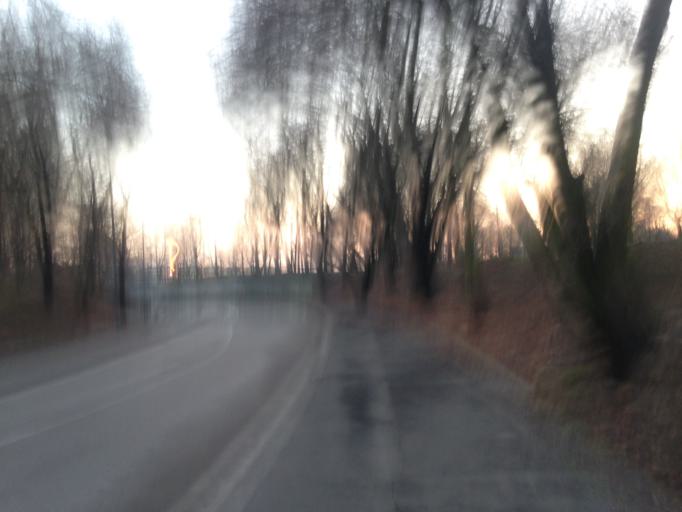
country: IT
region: Lombardy
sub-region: Citta metropolitana di Milano
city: Milano
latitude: 45.4323
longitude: 9.1649
